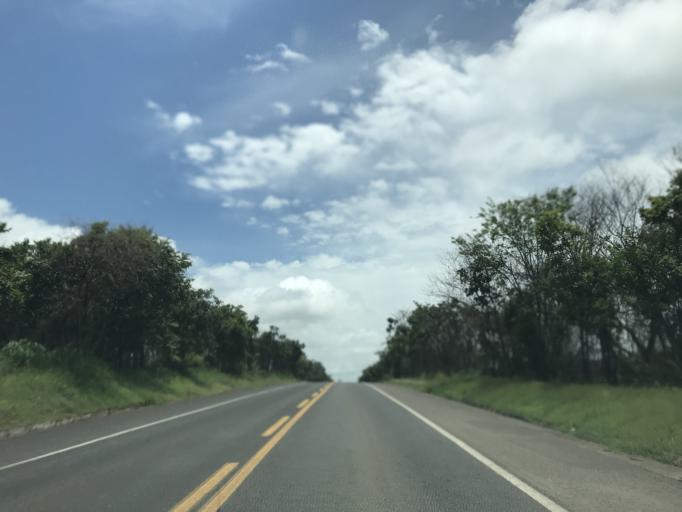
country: BR
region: Minas Gerais
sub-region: Prata
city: Prata
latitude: -19.6279
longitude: -48.9512
